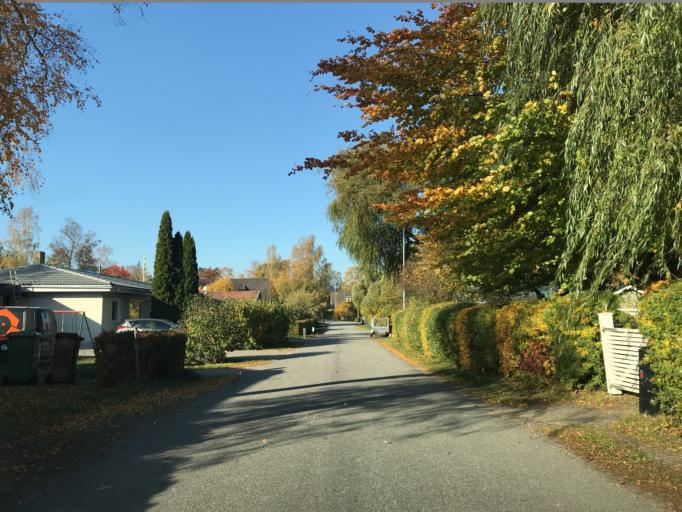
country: SE
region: Stockholm
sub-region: Sollentuna Kommun
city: Sollentuna
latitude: 59.4241
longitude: 17.9341
